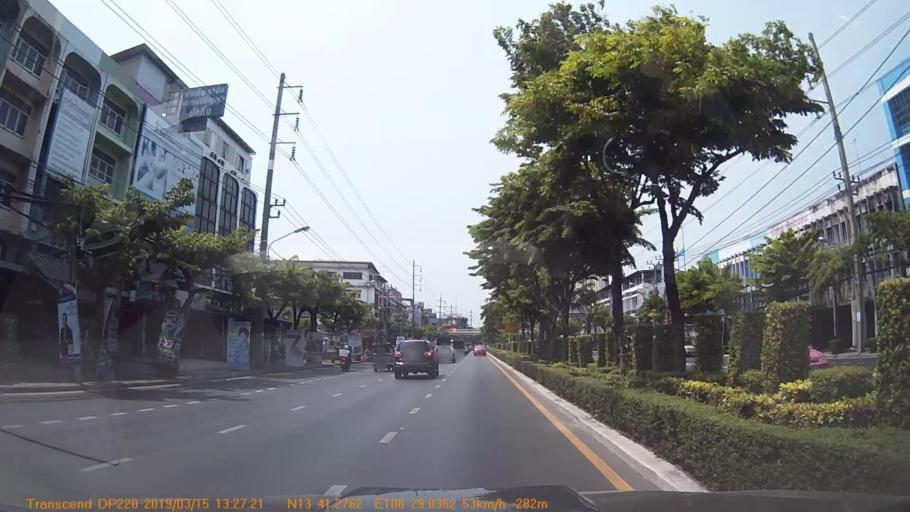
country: TH
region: Bangkok
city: Chom Thong
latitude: 13.6881
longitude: 100.4838
